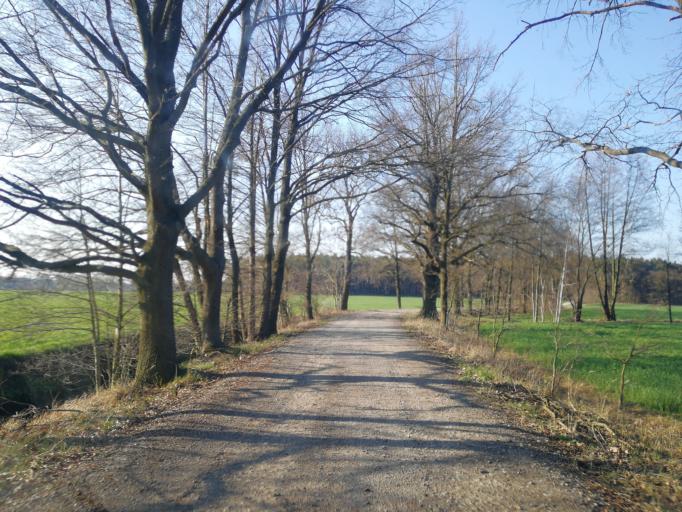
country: DE
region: Brandenburg
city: Drahnsdorf
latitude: 51.9330
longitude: 13.5841
